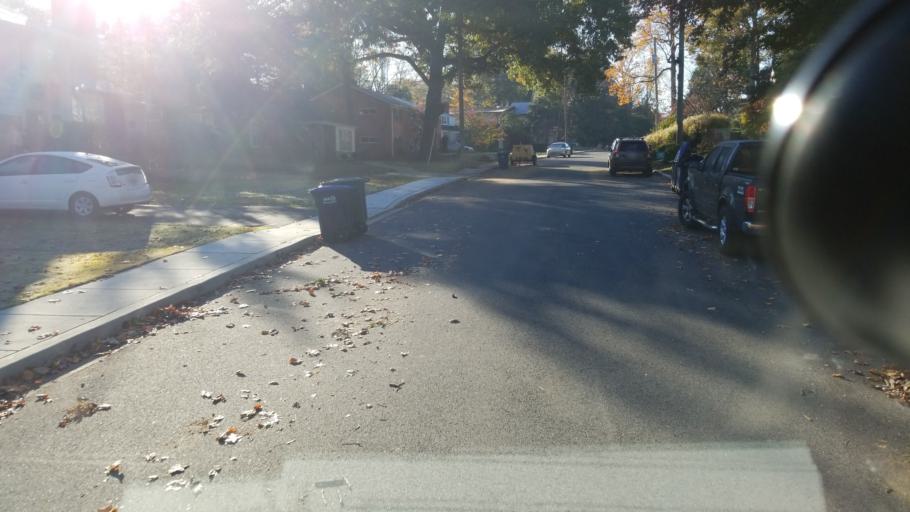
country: US
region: Maryland
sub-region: Montgomery County
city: Chevy Chase
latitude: 38.9831
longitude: -77.0562
